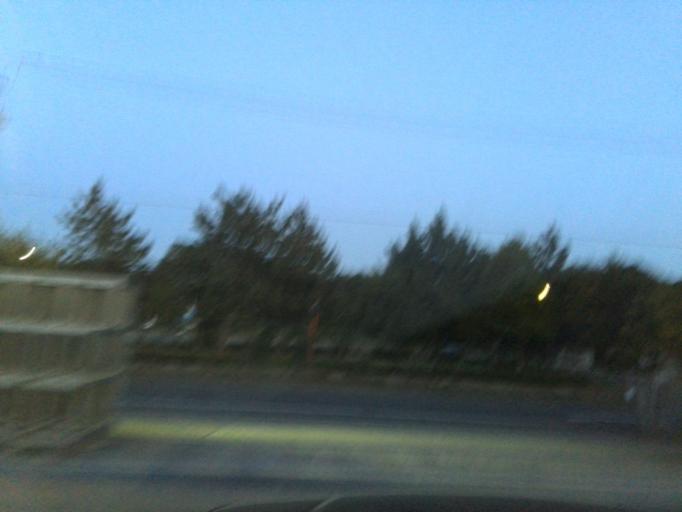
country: JP
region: Chiba
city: Funabashi
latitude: 35.6612
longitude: 140.0084
